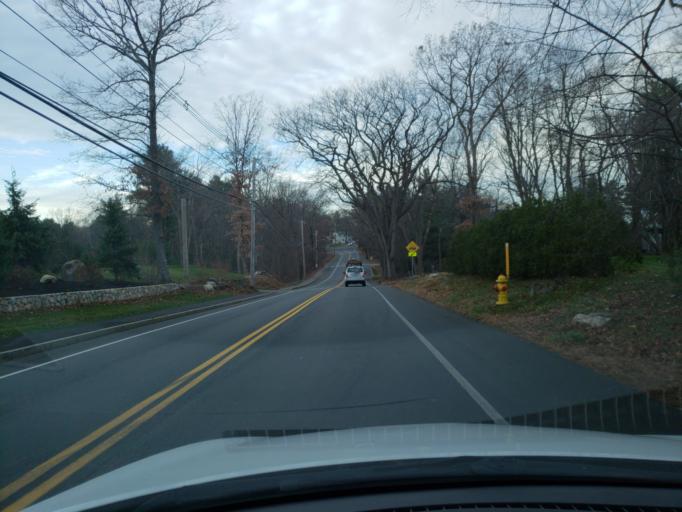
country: US
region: Massachusetts
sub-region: Essex County
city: Andover
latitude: 42.6664
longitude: -71.1719
